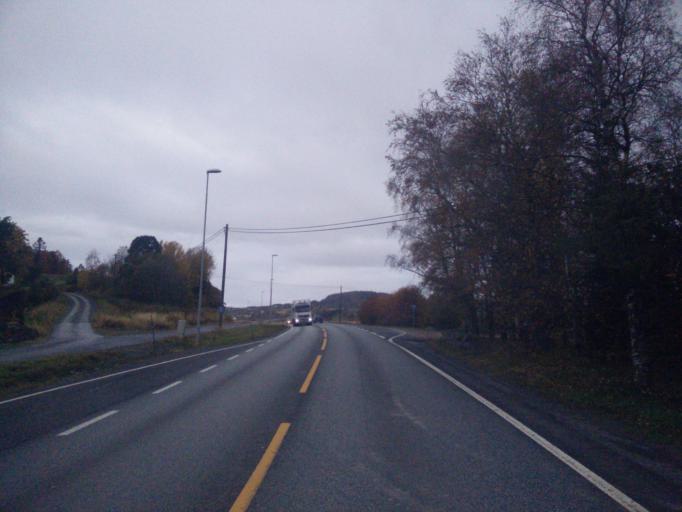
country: NO
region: Nord-Trondelag
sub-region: Stjordal
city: Stjordal
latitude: 63.4967
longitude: 10.8799
